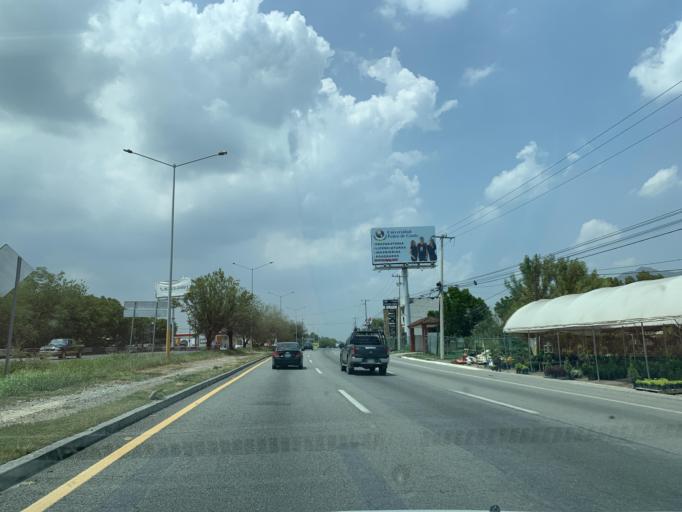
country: MX
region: Nuevo Leon
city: Santiago
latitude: 25.4595
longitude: -100.1691
